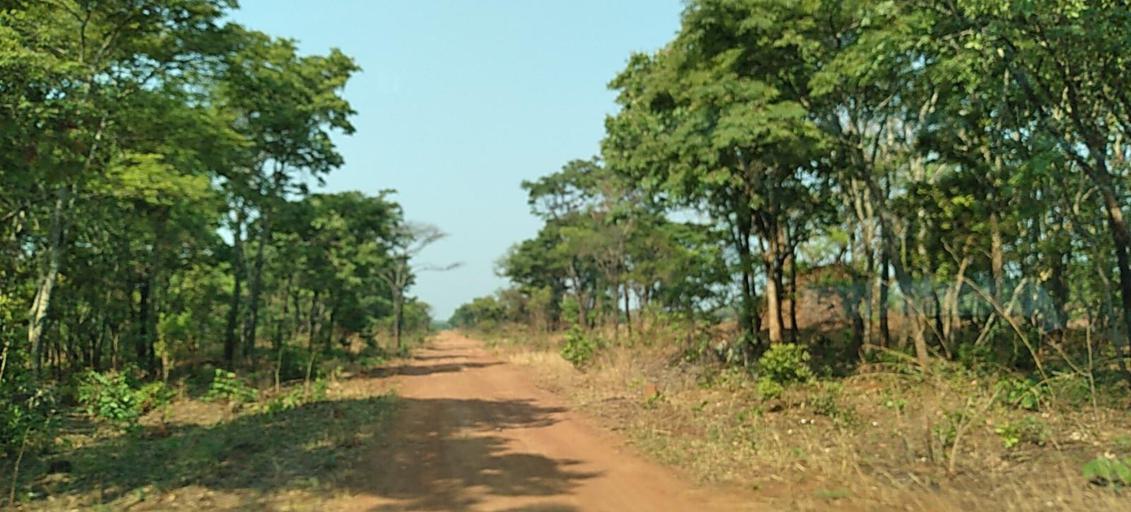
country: ZM
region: Copperbelt
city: Chingola
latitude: -12.8840
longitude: 27.4254
